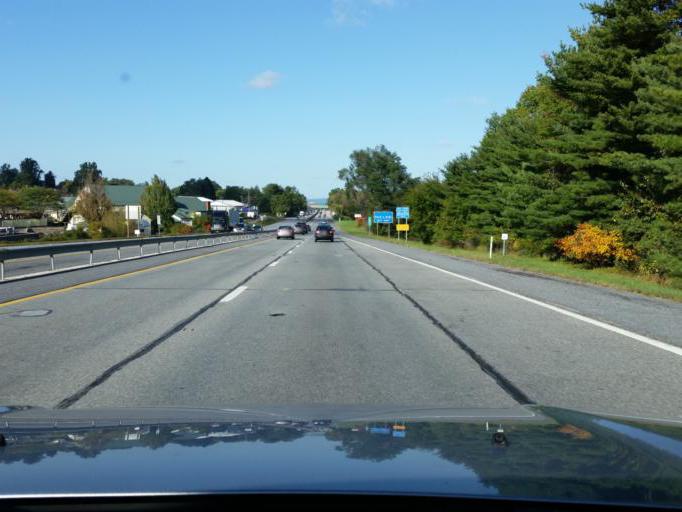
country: US
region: Pennsylvania
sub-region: Cumberland County
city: Mechanicsburg
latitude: 40.1825
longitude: -76.9845
